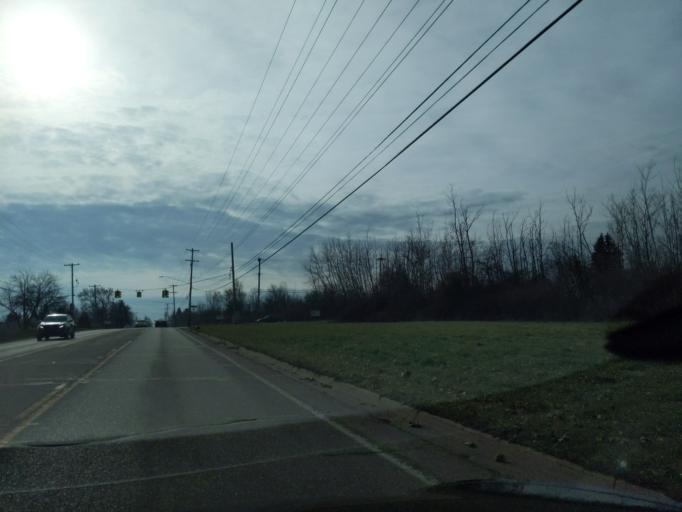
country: US
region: Michigan
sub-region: Ingham County
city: Holt
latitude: 42.6700
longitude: -84.5235
